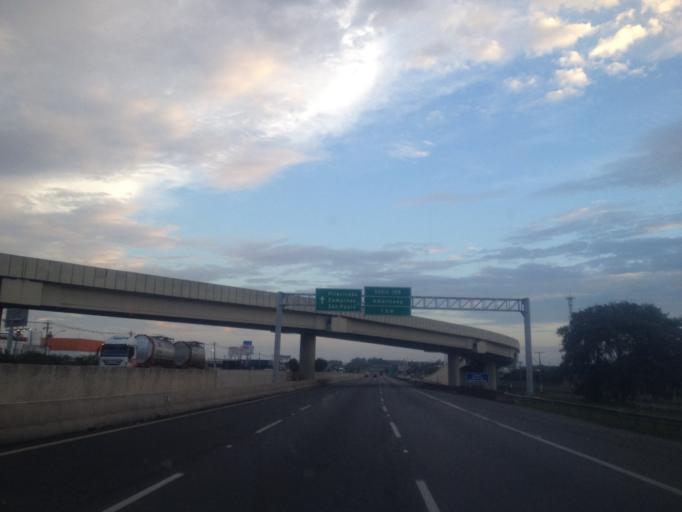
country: BR
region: Sao Paulo
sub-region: Americana
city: Americana
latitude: -22.7154
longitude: -47.2961
